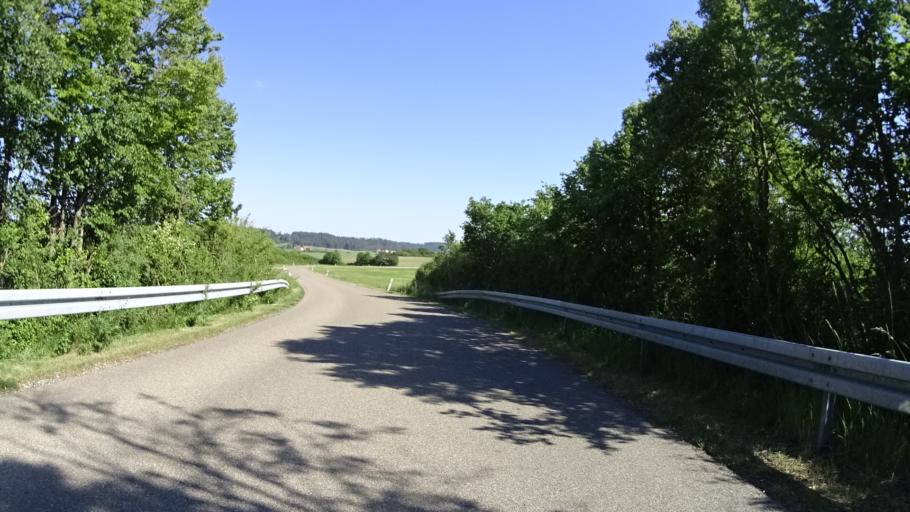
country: DE
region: Bavaria
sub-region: Regierungsbezirk Mittelfranken
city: Dombuhl
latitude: 49.2277
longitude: 10.2972
